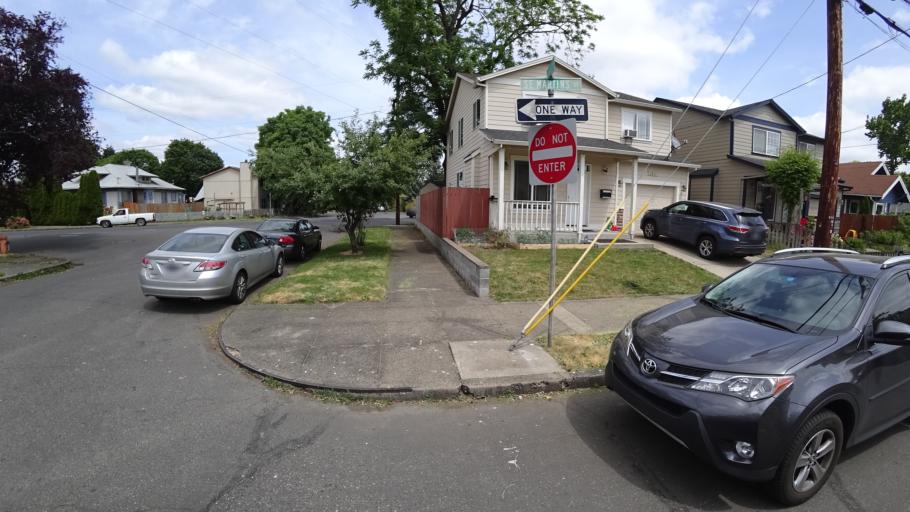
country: US
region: Oregon
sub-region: Multnomah County
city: Lents
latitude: 45.4790
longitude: -122.5918
